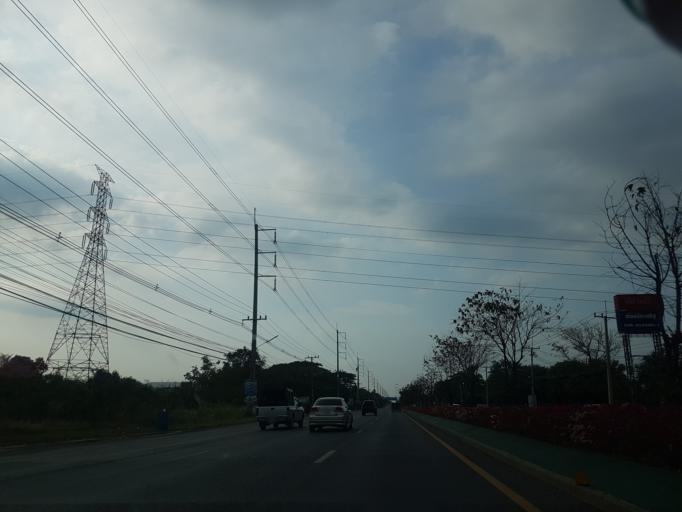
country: TH
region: Sara Buri
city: Phra Phutthabat
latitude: 14.7505
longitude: 100.7448
